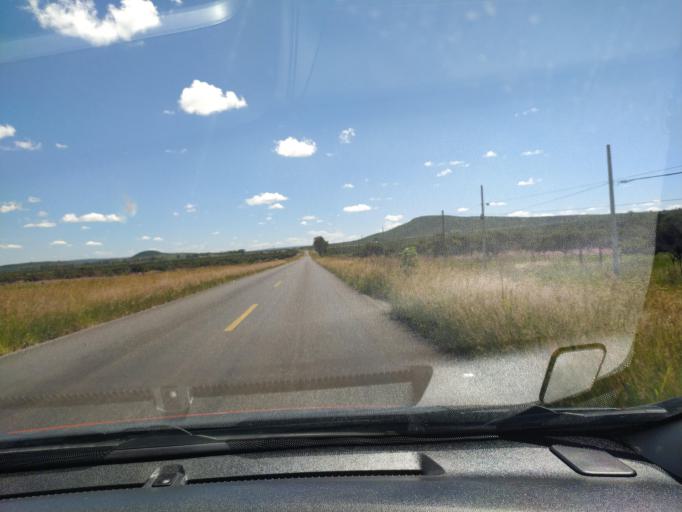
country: MX
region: Jalisco
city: San Miguel el Alto
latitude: 21.0167
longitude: -102.4863
